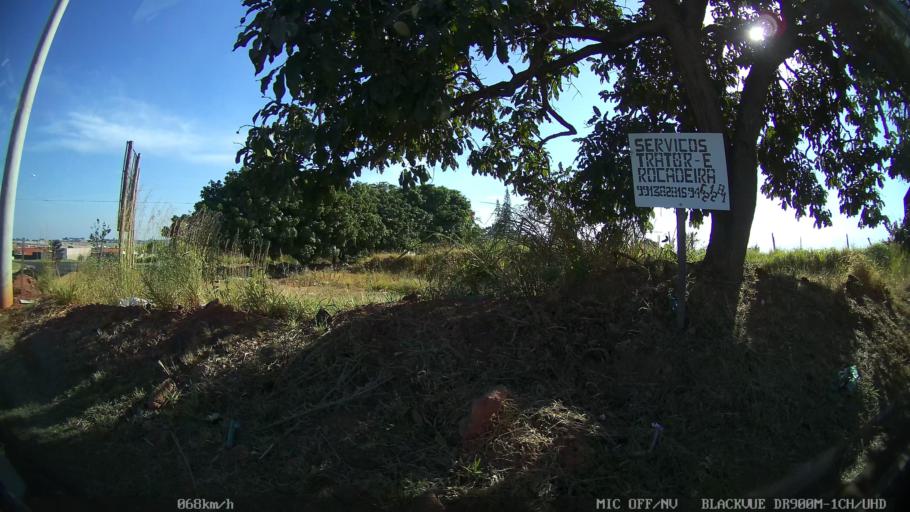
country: BR
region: Sao Paulo
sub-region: Franca
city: Franca
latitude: -20.5089
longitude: -47.4409
